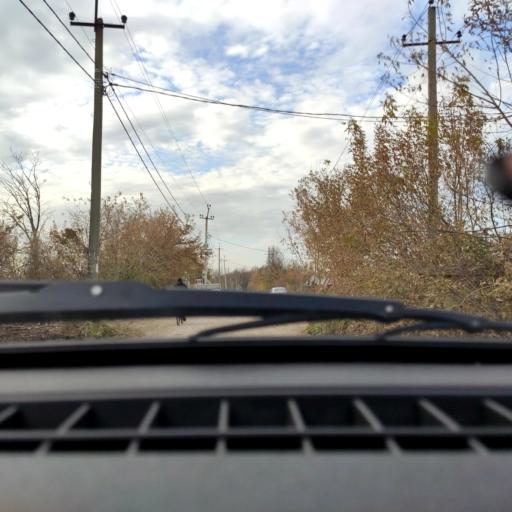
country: RU
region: Bashkortostan
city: Ufa
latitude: 54.7714
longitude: 55.9337
